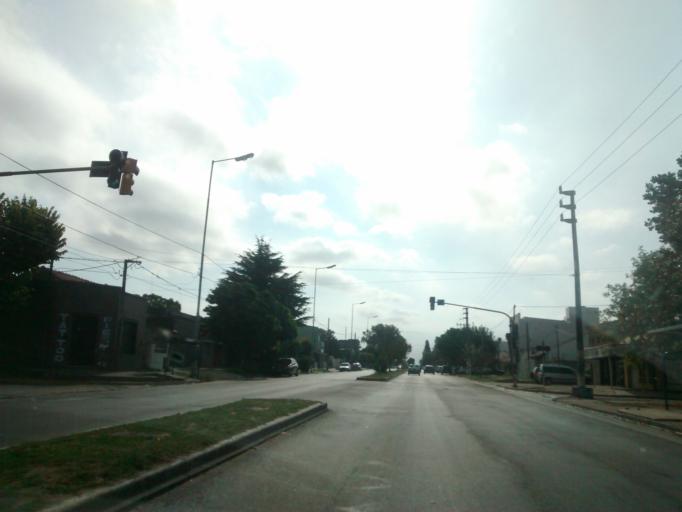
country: AR
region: Buenos Aires
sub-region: Partido de La Plata
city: La Plata
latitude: -34.9390
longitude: -57.9171
